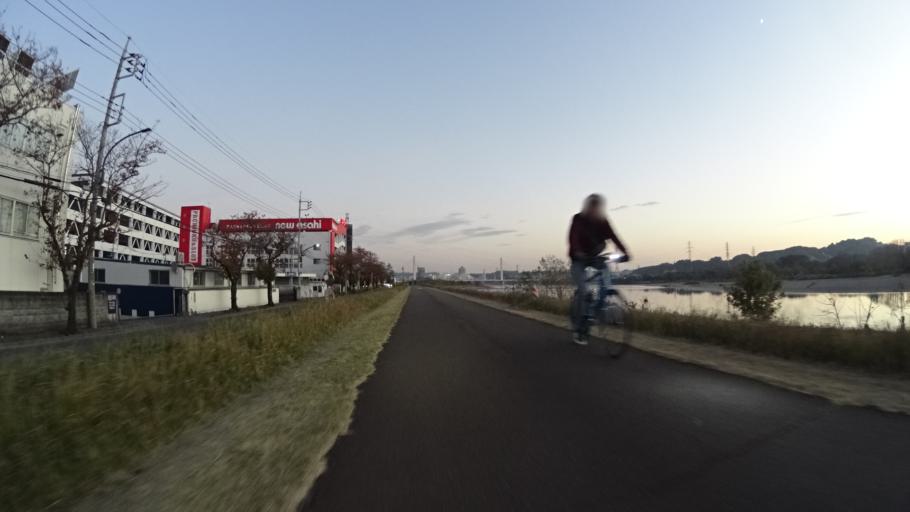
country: JP
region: Tokyo
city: Hino
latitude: 35.6682
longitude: 139.4337
